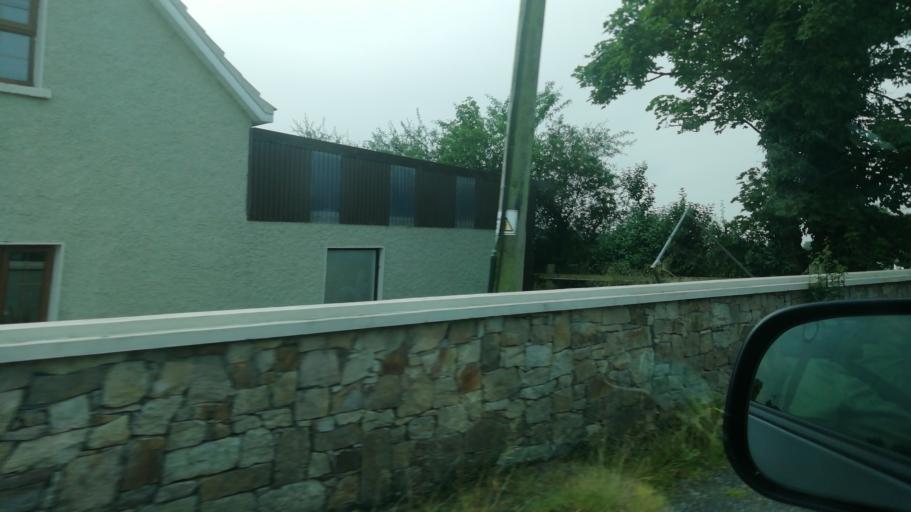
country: IE
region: Munster
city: Fethard
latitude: 52.5800
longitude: -7.6254
